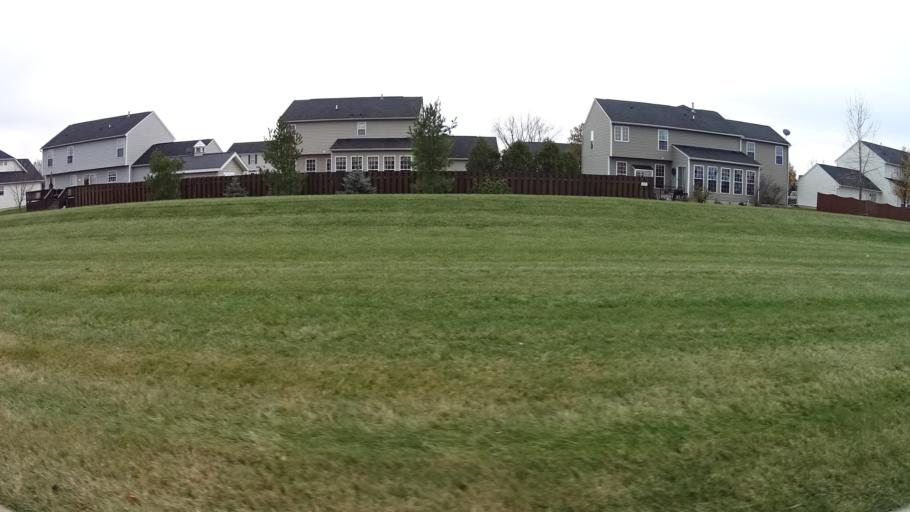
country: US
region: Ohio
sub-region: Lorain County
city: North Ridgeville
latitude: 41.4096
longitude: -82.0477
